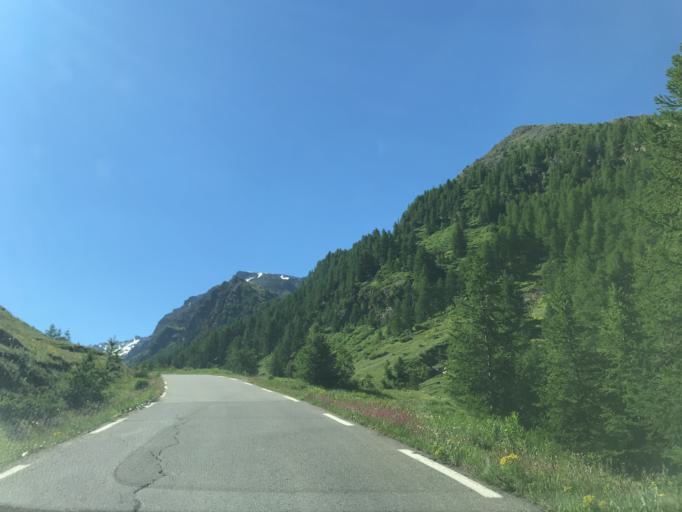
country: IT
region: Piedmont
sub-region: Provincia di Cuneo
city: Pontechianale
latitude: 44.7092
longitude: 6.9229
